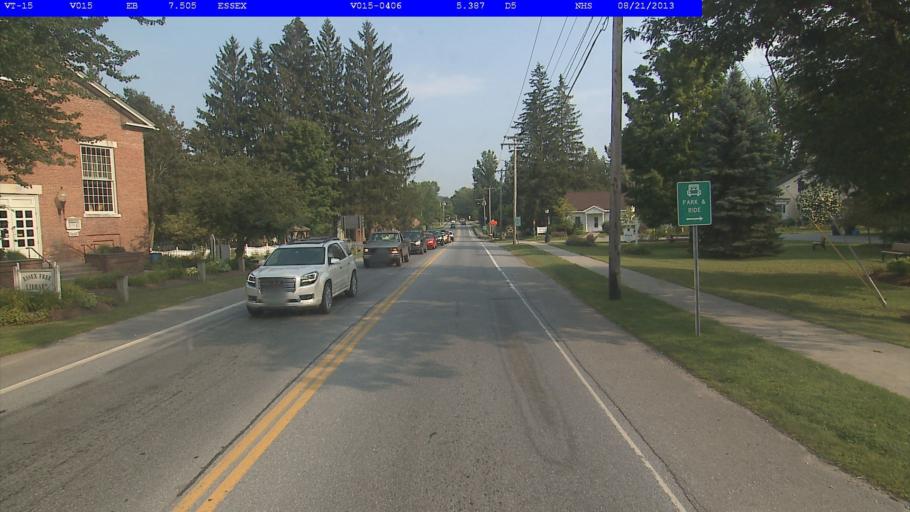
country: US
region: Vermont
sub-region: Chittenden County
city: Essex Junction
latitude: 44.5116
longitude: -73.0590
